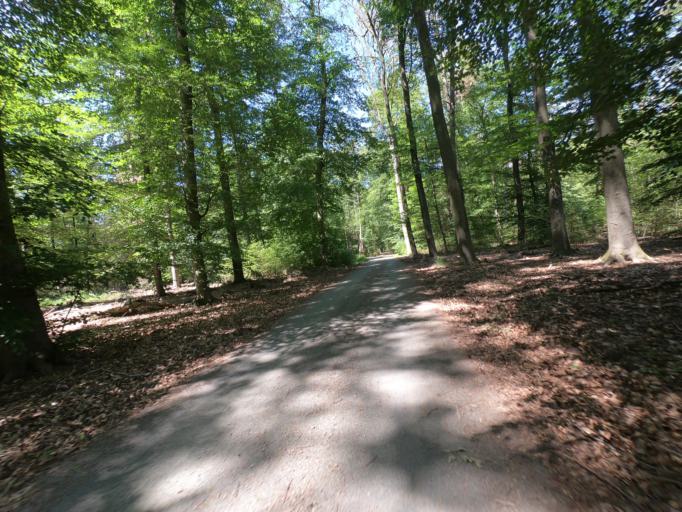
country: DE
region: Hesse
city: Niederrad
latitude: 50.0415
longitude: 8.6411
